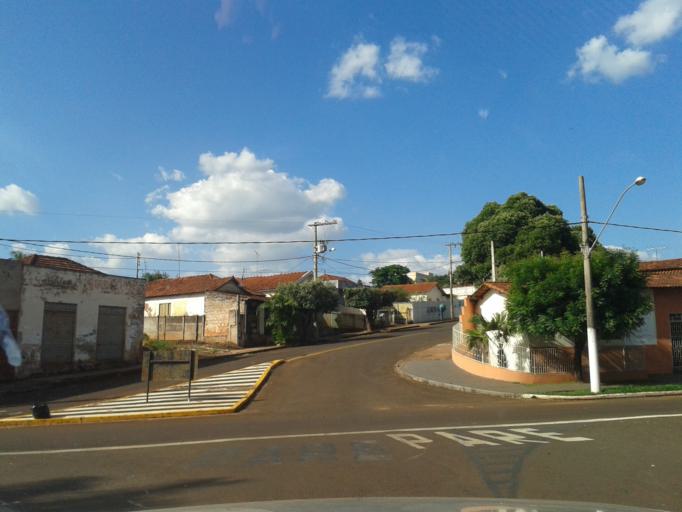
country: BR
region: Minas Gerais
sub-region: Ituiutaba
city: Ituiutaba
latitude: -18.9703
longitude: -49.4578
